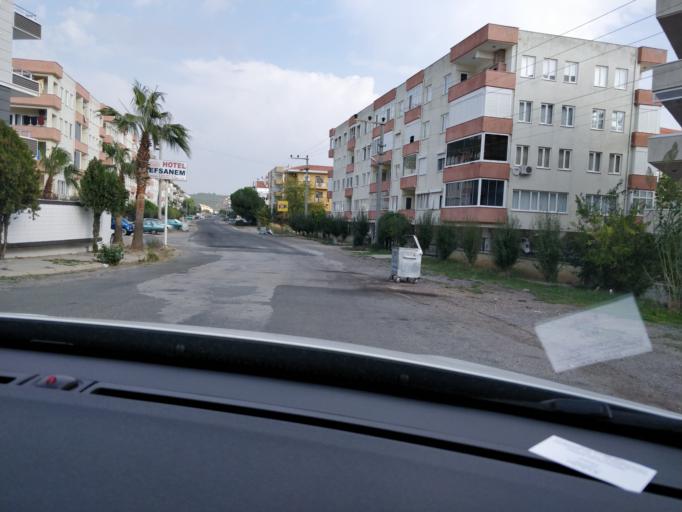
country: TR
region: Balikesir
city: Ayvalik
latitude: 39.2732
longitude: 26.6516
